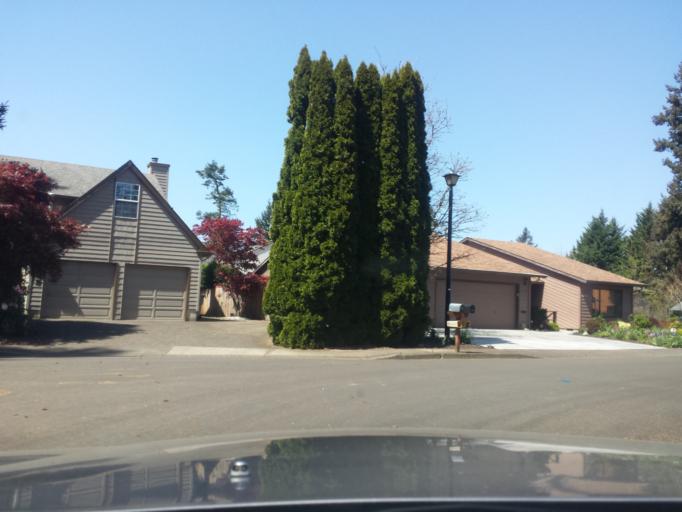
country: US
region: Oregon
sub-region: Washington County
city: Aloha
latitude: 45.4843
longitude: -122.8591
